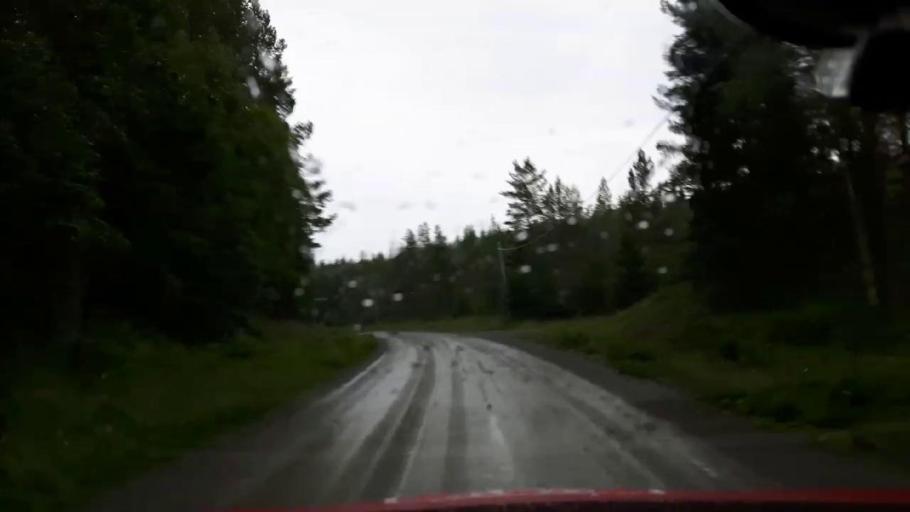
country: SE
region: Jaemtland
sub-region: OEstersunds Kommun
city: Brunflo
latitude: 62.8958
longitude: 14.8690
